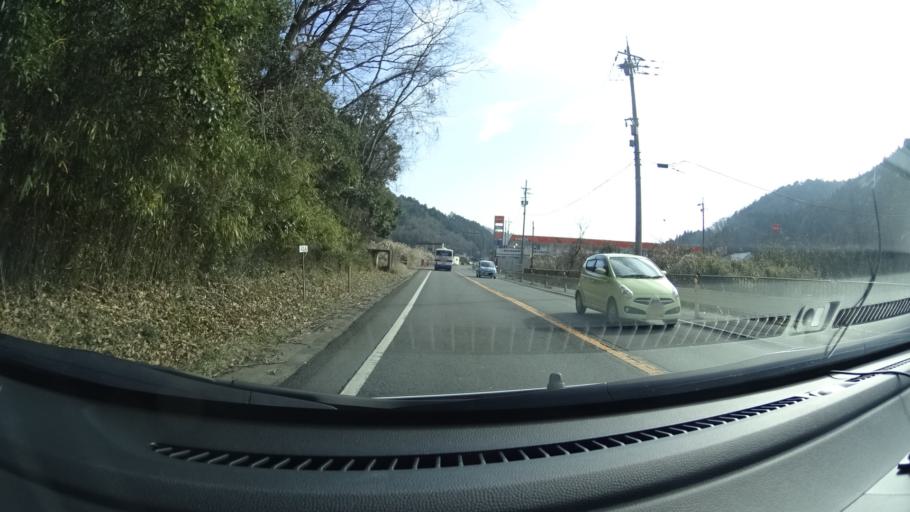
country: JP
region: Kyoto
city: Kameoka
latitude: 35.1360
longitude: 135.4266
